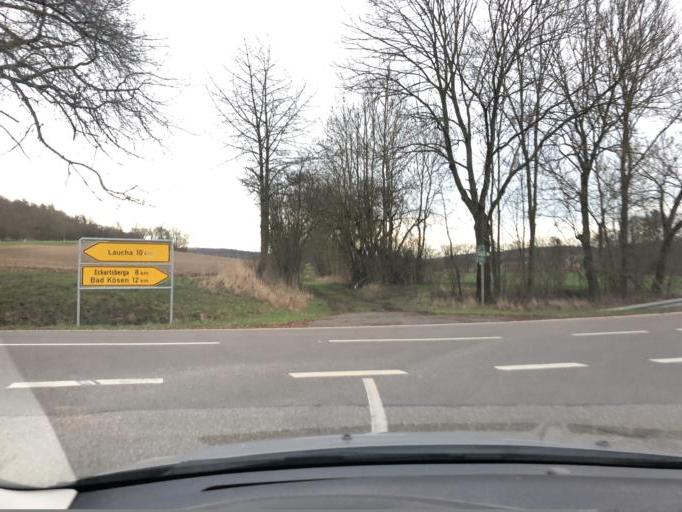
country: DE
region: Saxony-Anhalt
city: Bad Bibra
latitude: 51.1710
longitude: 11.6099
